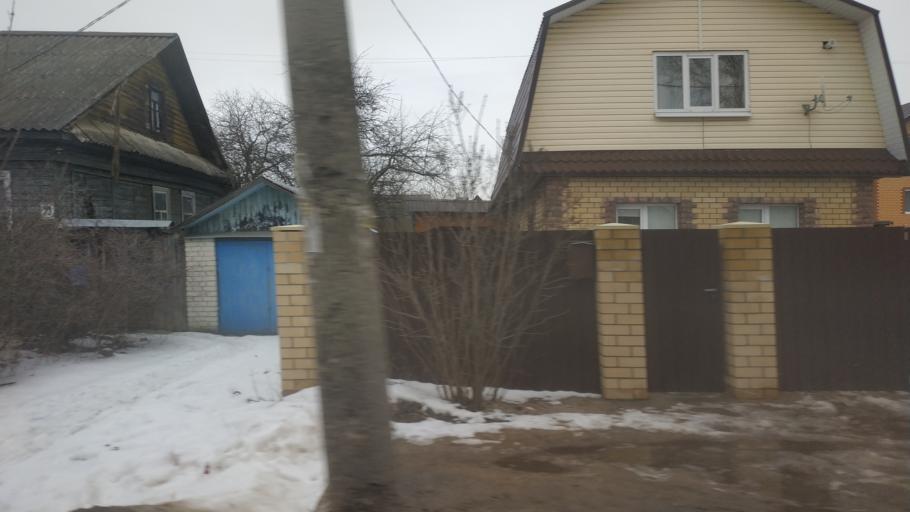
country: RU
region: Tverskaya
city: Tver
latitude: 56.8916
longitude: 35.8520
